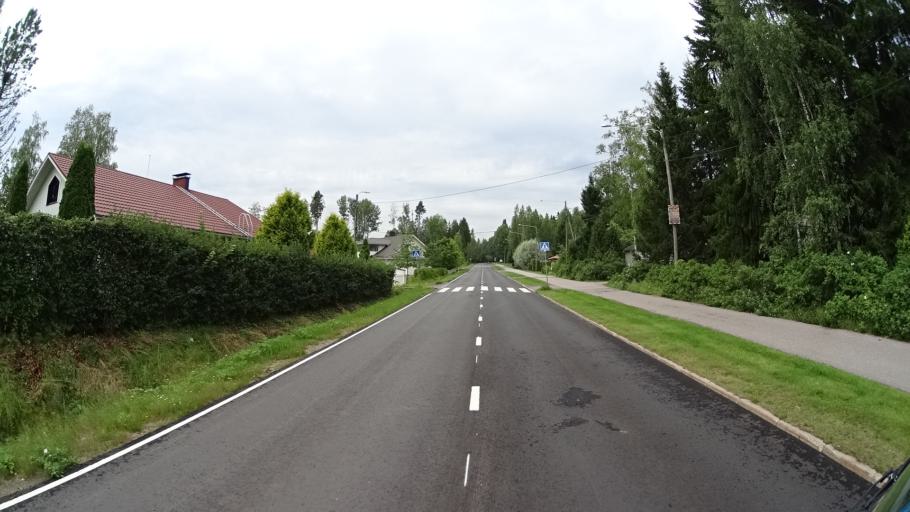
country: FI
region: Uusimaa
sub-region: Helsinki
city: Kilo
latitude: 60.2401
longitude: 24.7665
